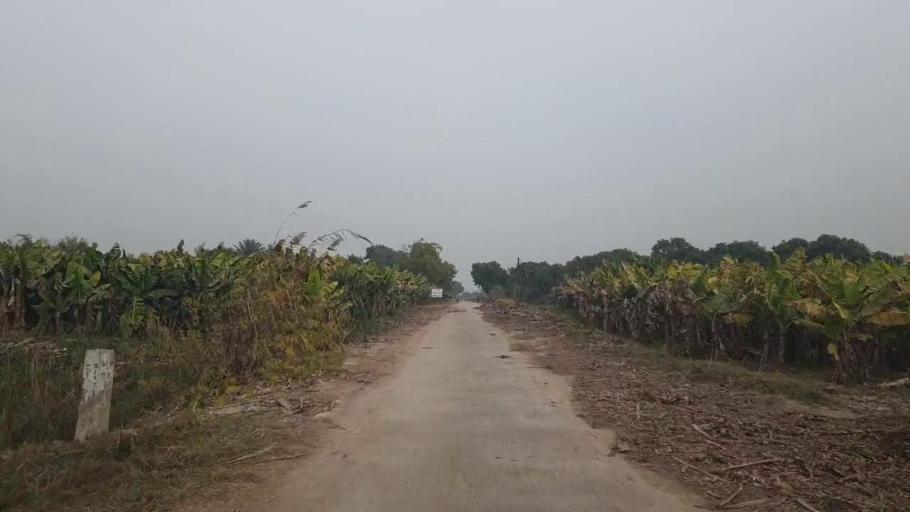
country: PK
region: Sindh
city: Tando Adam
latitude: 25.8426
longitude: 68.6575
